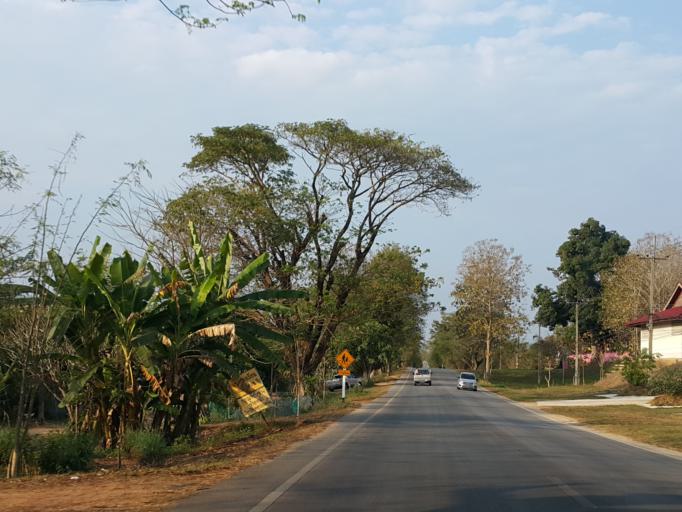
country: TH
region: Lampang
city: Lampang
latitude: 18.5039
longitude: 99.4728
